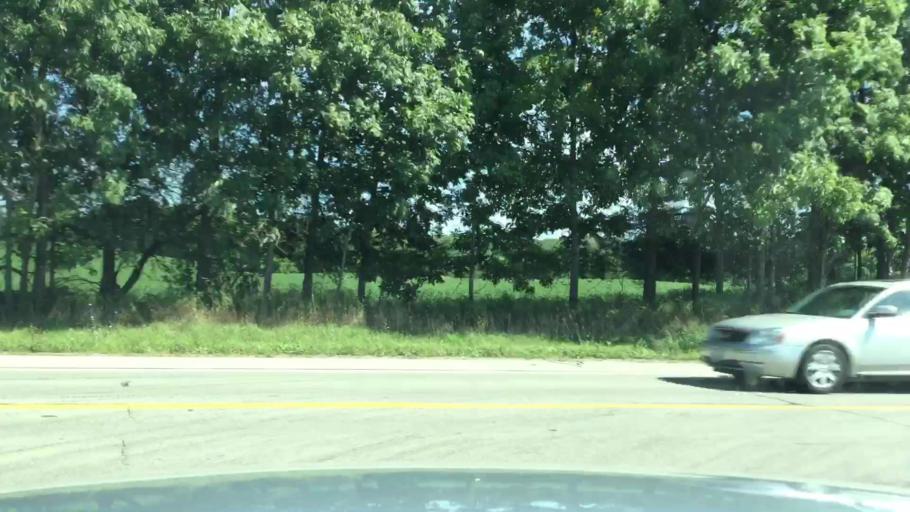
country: US
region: Michigan
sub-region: Lenawee County
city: Manitou Beach-Devils Lake
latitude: 42.0112
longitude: -84.3055
